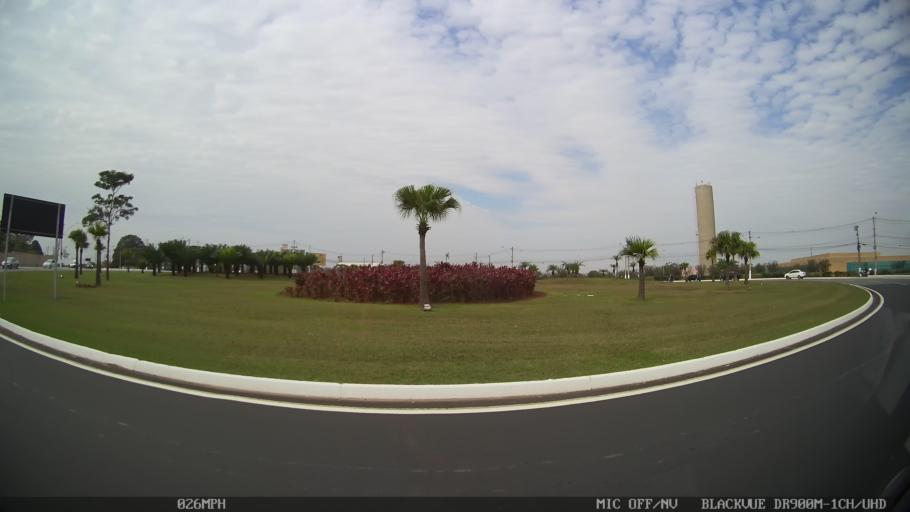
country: BR
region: Sao Paulo
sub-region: Paulinia
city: Paulinia
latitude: -22.7824
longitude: -47.1586
